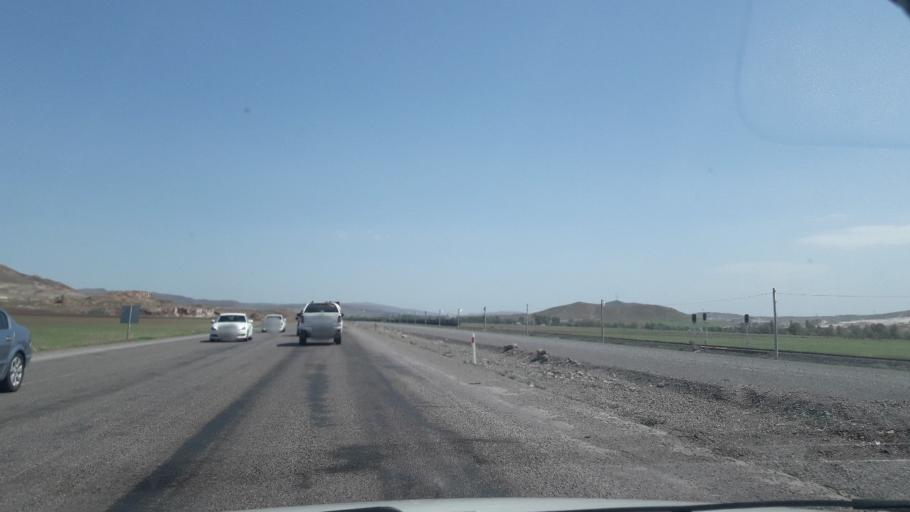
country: TR
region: Sivas
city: Ulas
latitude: 39.5311
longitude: 37.0156
